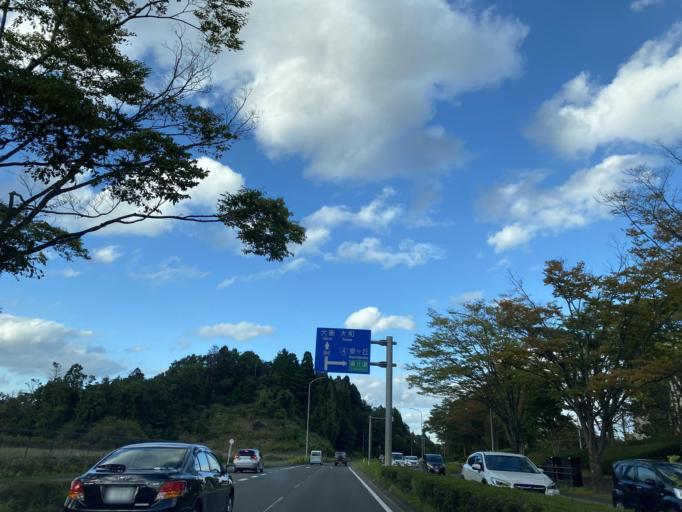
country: JP
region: Miyagi
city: Tomiya
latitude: 38.3537
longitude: 140.8430
